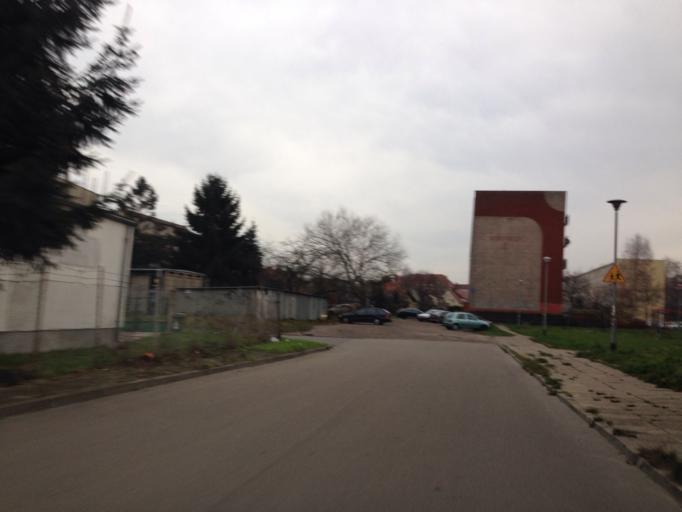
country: PL
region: Pomeranian Voivodeship
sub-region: Gdansk
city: Gdansk
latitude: 54.3897
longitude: 18.6291
